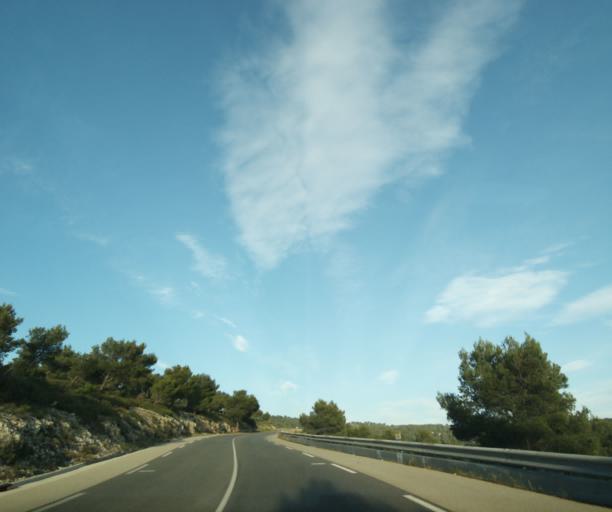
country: FR
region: Provence-Alpes-Cote d'Azur
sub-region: Departement des Bouches-du-Rhone
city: Roquefort-la-Bedoule
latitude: 43.2306
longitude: 5.5876
